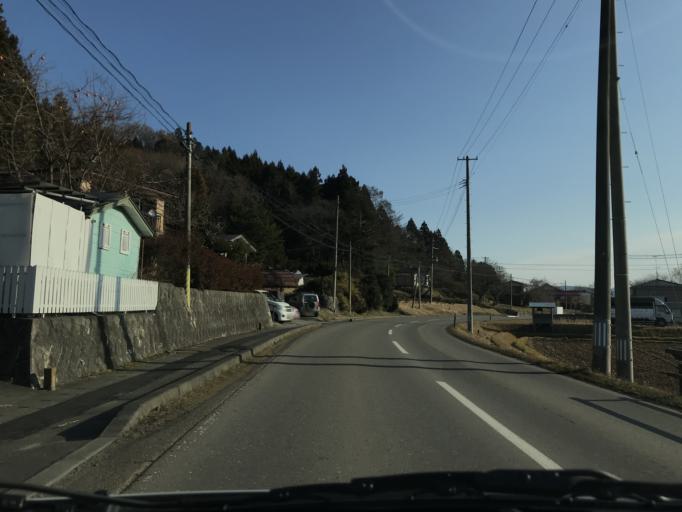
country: JP
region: Iwate
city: Ichinoseki
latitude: 38.9781
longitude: 141.0998
